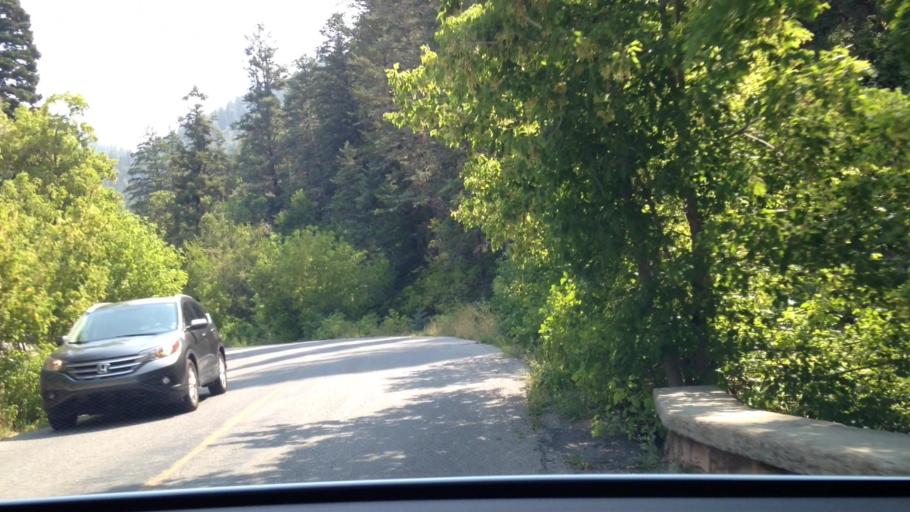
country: US
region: Utah
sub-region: Salt Lake County
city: Mount Olympus
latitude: 40.7000
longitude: -111.7039
